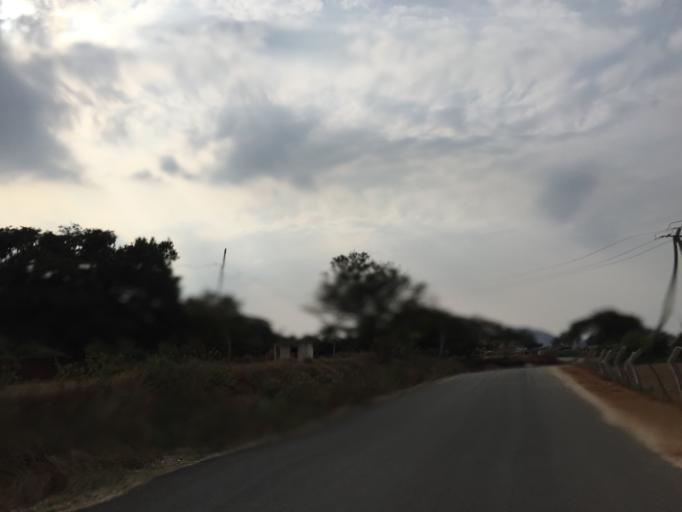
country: IN
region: Karnataka
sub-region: Chikkaballapur
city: Gudibanda
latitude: 13.5667
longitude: 77.7336
